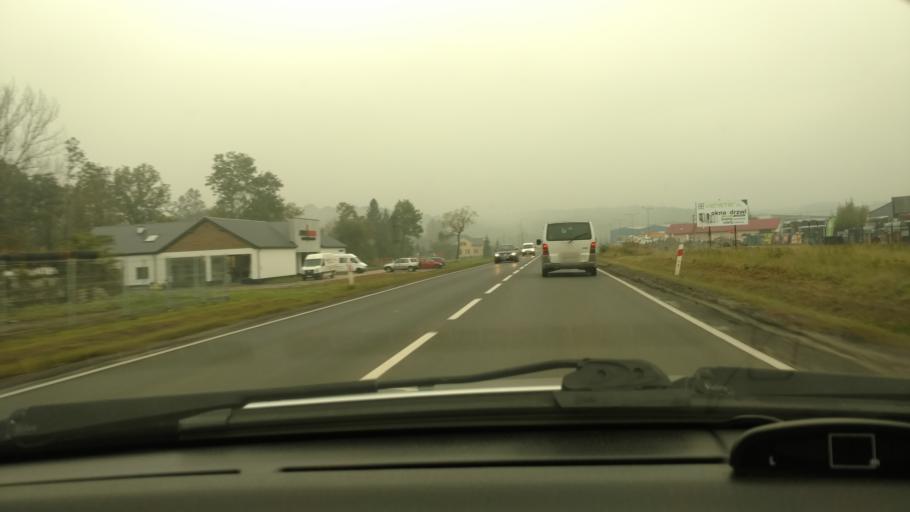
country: PL
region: Lesser Poland Voivodeship
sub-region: Powiat gorlicki
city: Kobylanka
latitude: 49.6825
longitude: 21.1903
